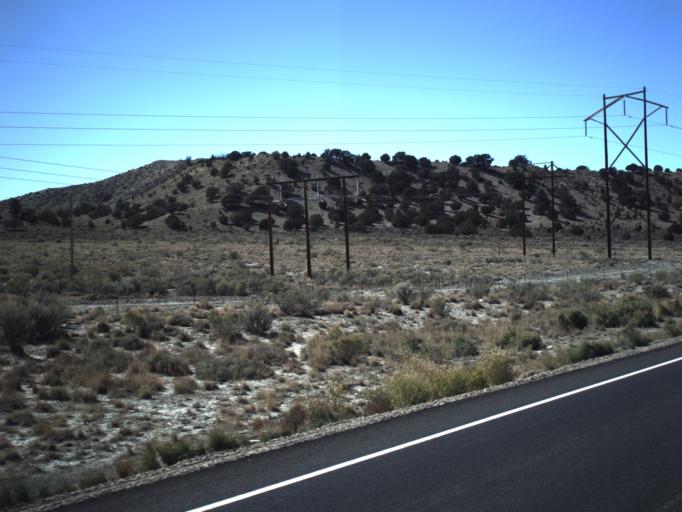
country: US
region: Utah
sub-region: Garfield County
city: Panguitch
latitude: 37.5993
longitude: -111.9534
